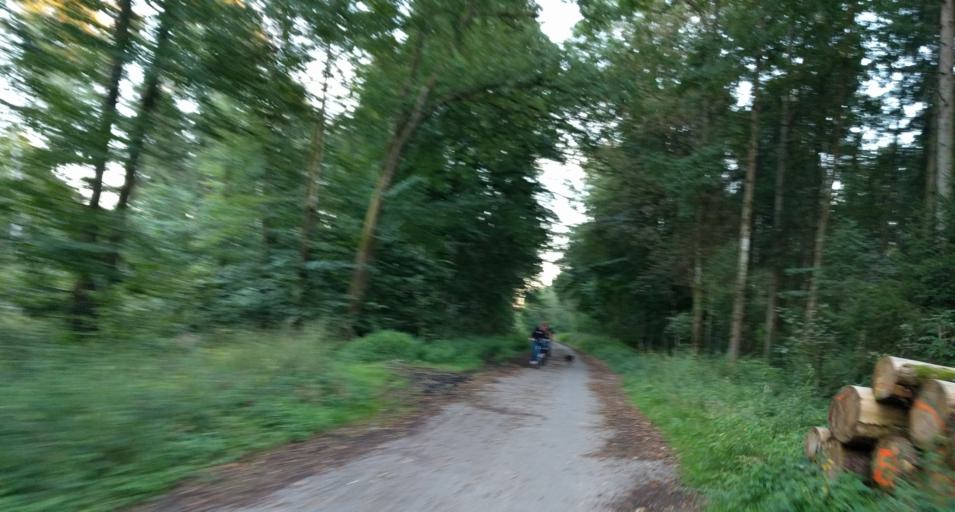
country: DE
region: Bavaria
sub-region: Upper Bavaria
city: Oberhaching
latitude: 48.0262
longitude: 11.5678
